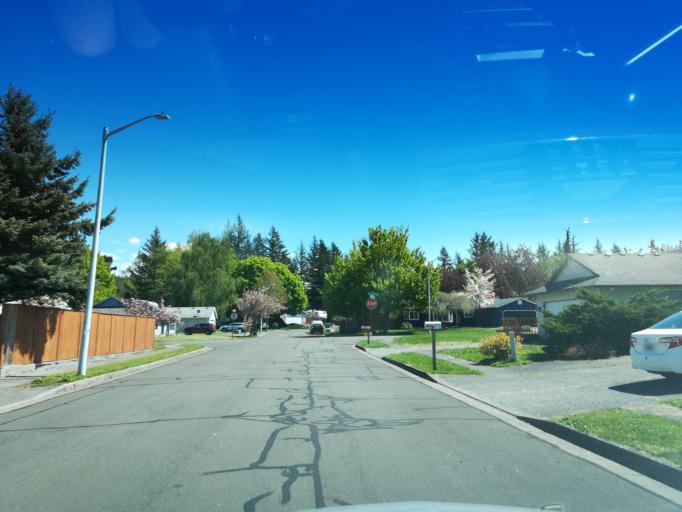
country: US
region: Oregon
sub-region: Multnomah County
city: Troutdale
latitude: 45.5268
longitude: -122.3768
